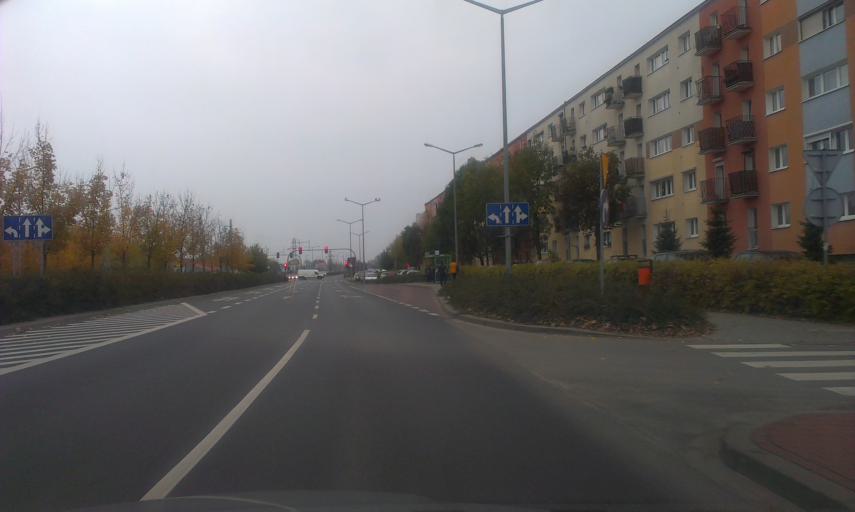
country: PL
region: Greater Poland Voivodeship
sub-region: Poznan
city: Poznan
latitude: 52.4068
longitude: 16.8678
